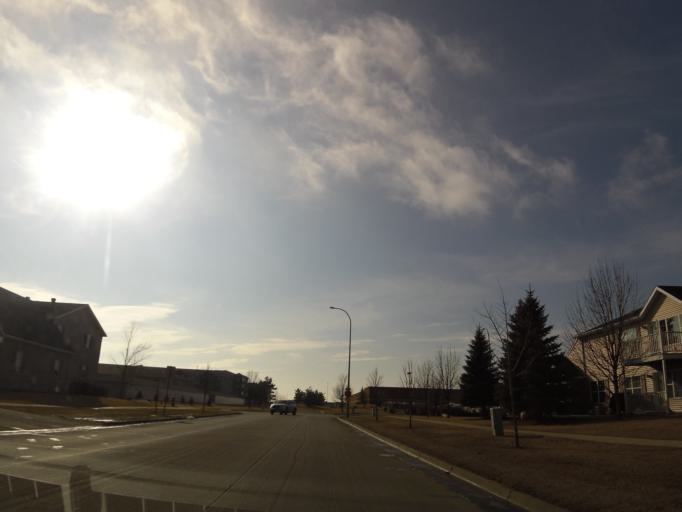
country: US
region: North Dakota
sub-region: Grand Forks County
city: Grand Forks
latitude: 47.8859
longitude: -97.0766
